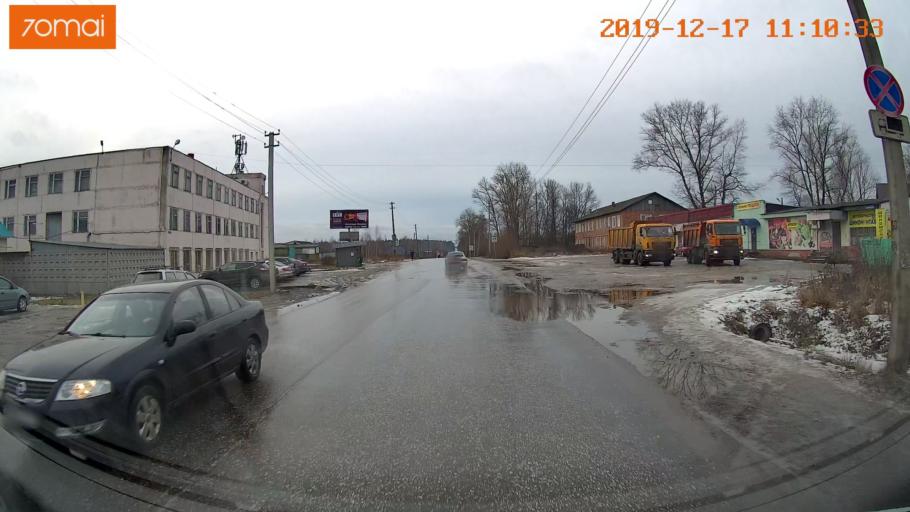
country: RU
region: Vladimir
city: Gus'-Khrustal'nyy
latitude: 55.5919
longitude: 40.6409
